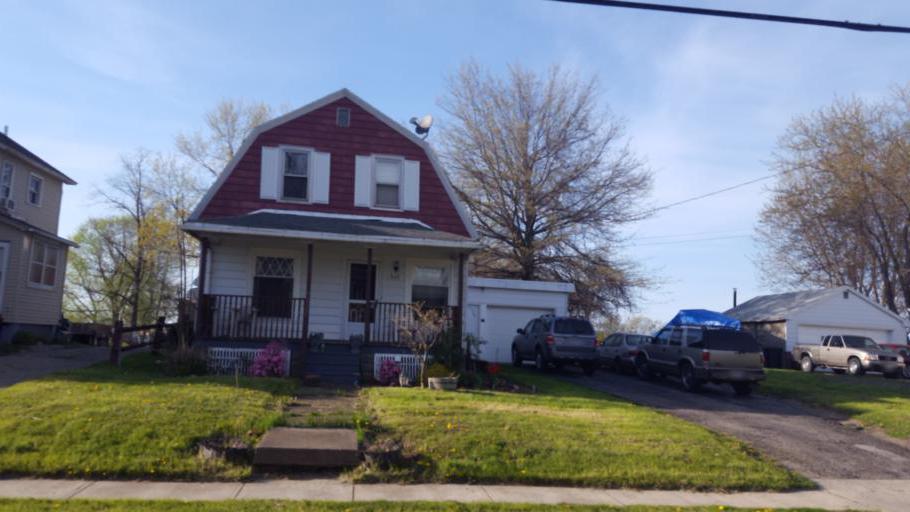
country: US
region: Ohio
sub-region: Ashtabula County
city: Edgewood
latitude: 41.9002
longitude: -80.7884
